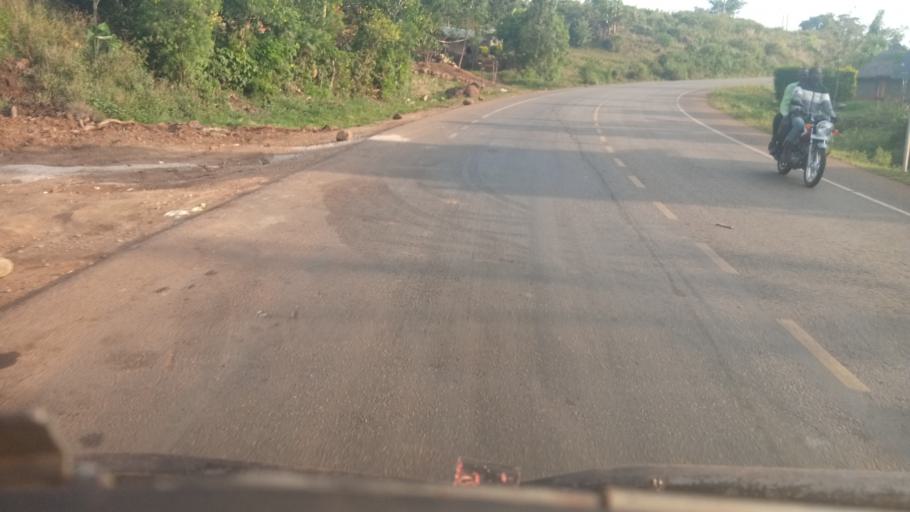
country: UG
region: Eastern Region
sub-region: Sironko District
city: Sironko
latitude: 1.3366
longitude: 34.3229
